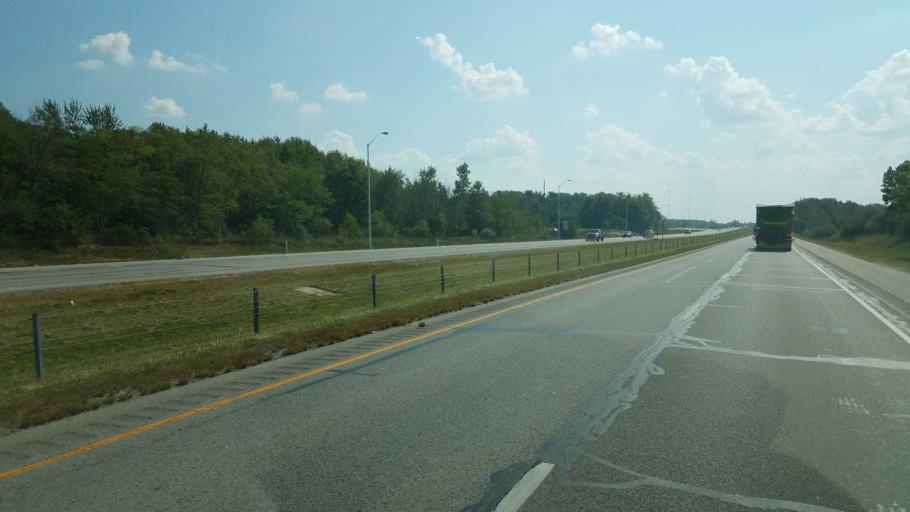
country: US
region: Indiana
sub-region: DeKalb County
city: Garrett
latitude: 41.3033
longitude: -85.0872
